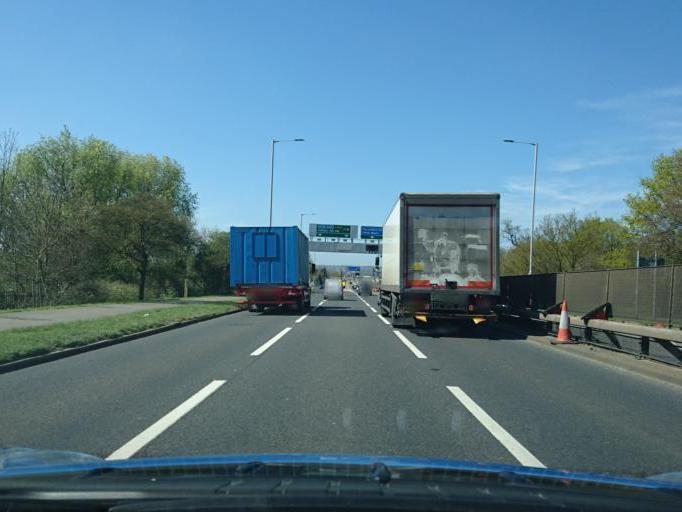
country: GB
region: England
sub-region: Greater London
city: Hendon
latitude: 51.5992
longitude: -0.2265
